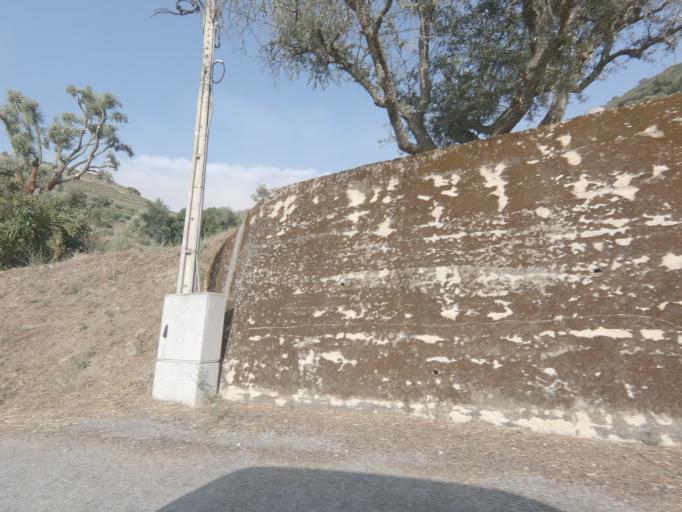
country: PT
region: Viseu
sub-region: Tabuaco
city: Tabuaco
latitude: 41.1301
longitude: -7.5328
